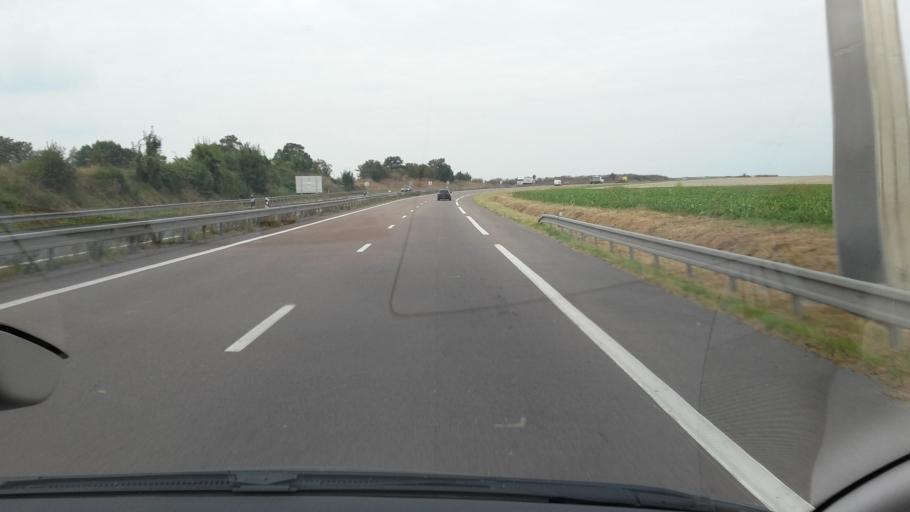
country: FR
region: Champagne-Ardenne
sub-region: Departement de la Marne
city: Warmeriville
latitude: 49.3607
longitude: 4.2081
